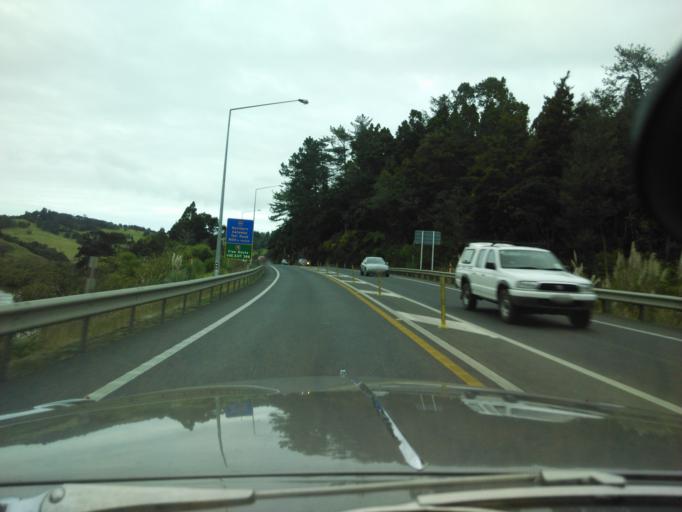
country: NZ
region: Auckland
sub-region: Auckland
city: Warkworth
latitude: -36.5232
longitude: 174.6761
